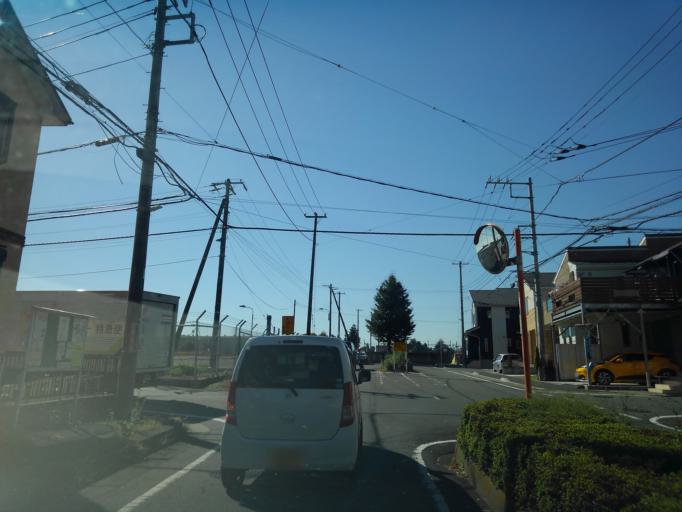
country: JP
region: Tokyo
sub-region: Machida-shi
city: Machida
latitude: 35.5864
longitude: 139.3863
